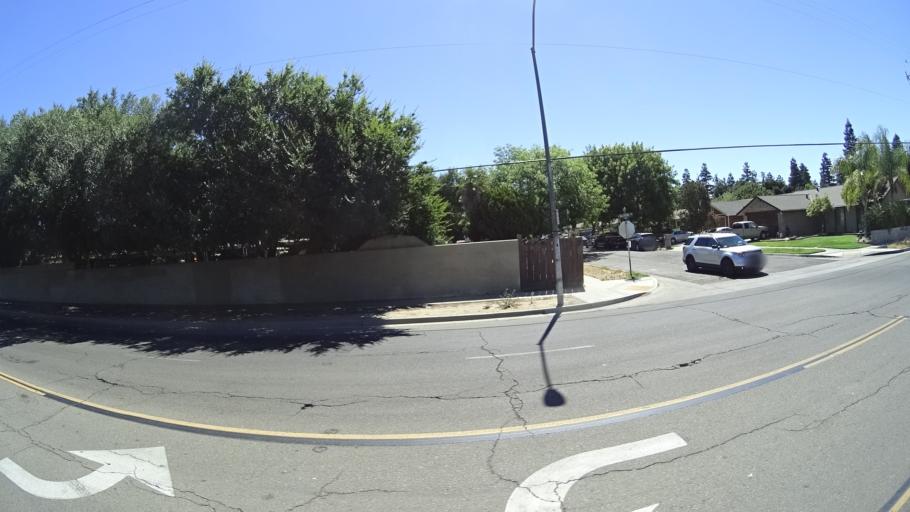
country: US
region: California
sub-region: Fresno County
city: West Park
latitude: 36.7980
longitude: -119.8534
